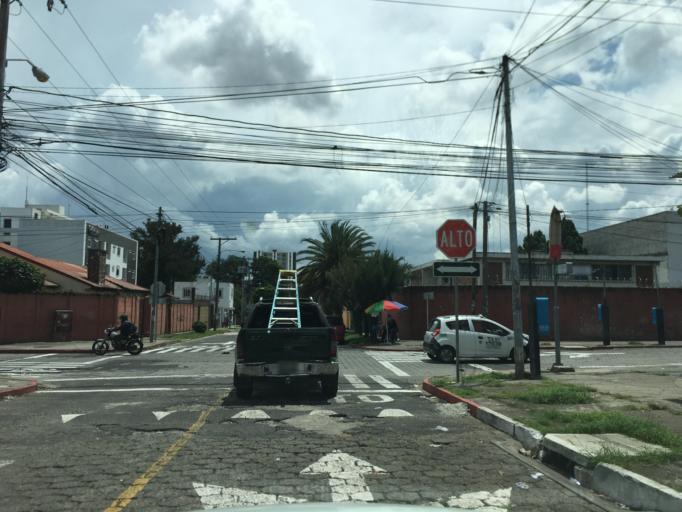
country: GT
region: Guatemala
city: Santa Catarina Pinula
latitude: 14.5873
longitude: -90.5445
